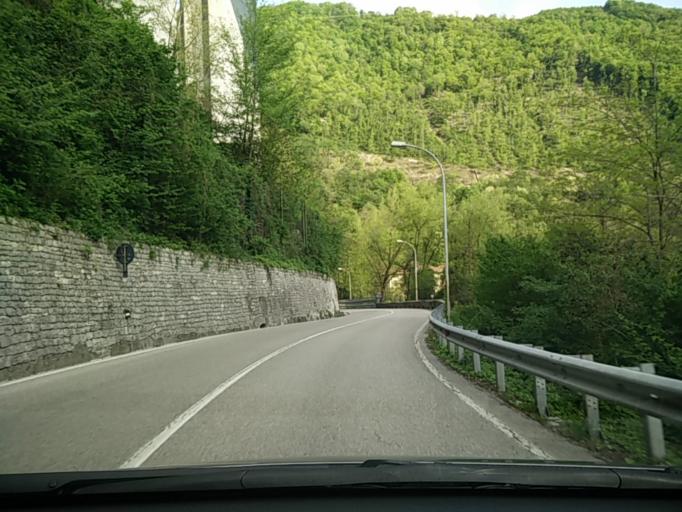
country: IT
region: Veneto
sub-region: Provincia di Treviso
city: Fregona
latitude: 46.0304
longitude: 12.3020
